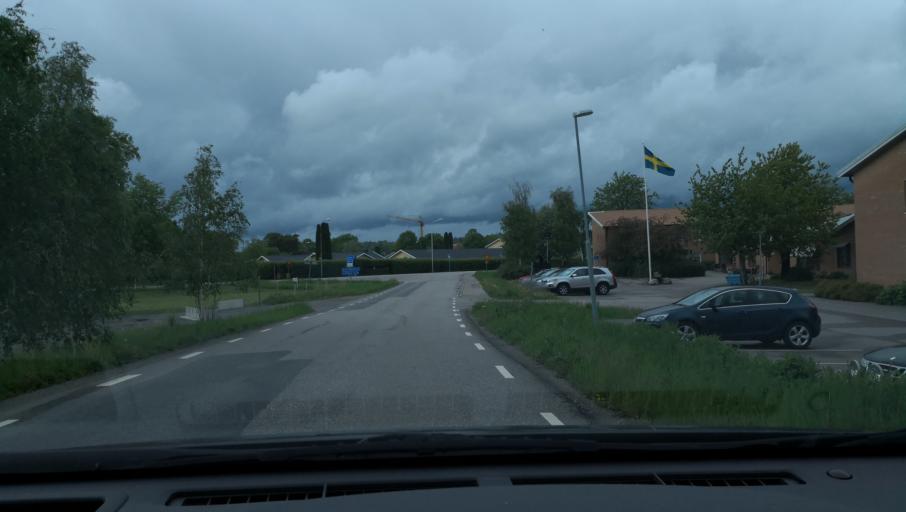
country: SE
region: Uppsala
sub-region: Enkopings Kommun
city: Orsundsbro
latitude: 59.7304
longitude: 17.3062
